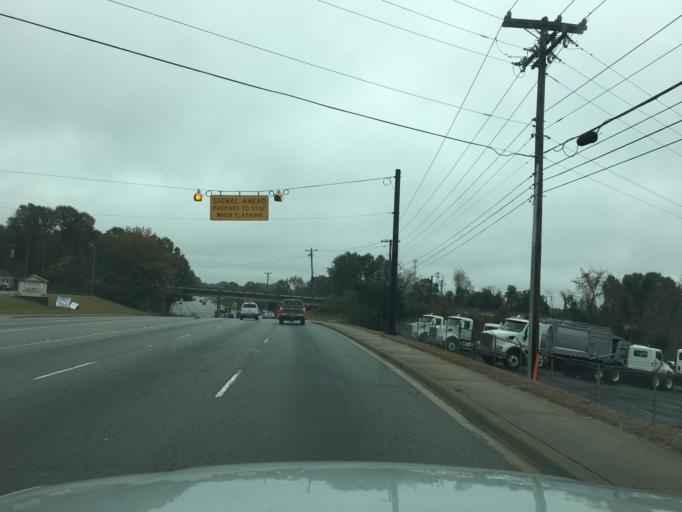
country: US
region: South Carolina
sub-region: Greenville County
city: Gantt
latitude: 34.8026
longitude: -82.4294
